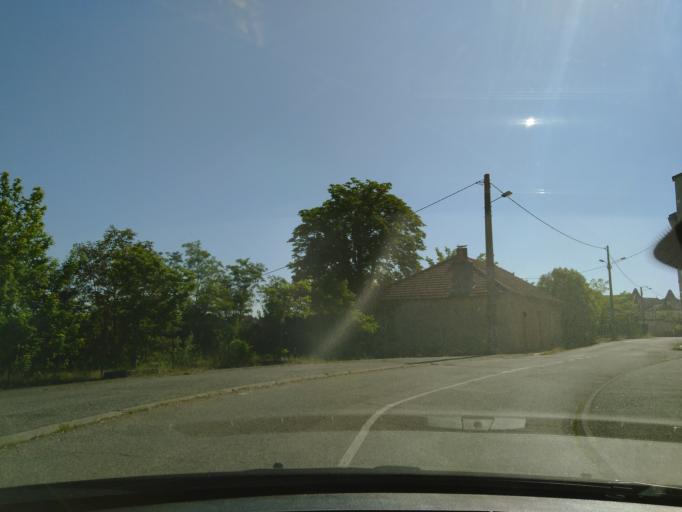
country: FR
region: Midi-Pyrenees
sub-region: Departement du Gers
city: Gimont
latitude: 43.6246
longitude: 0.8754
